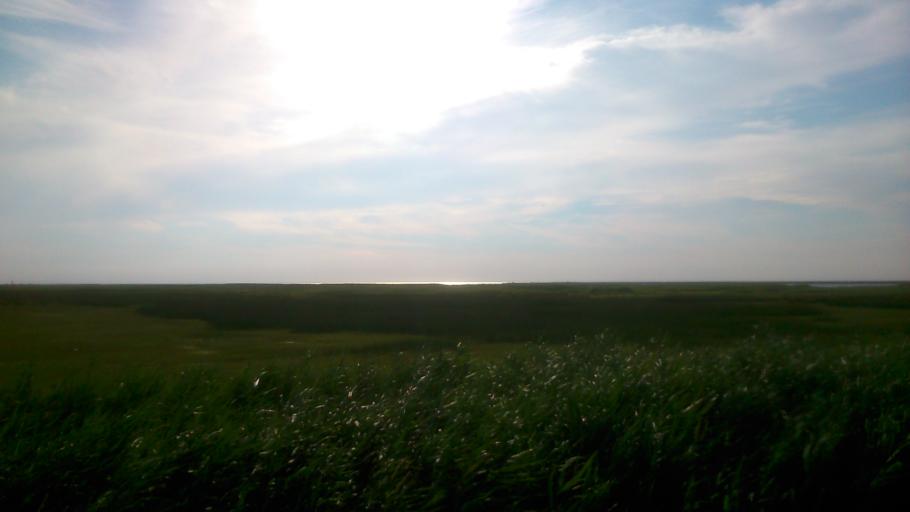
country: DK
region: Central Jutland
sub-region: Ringkobing-Skjern Kommune
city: Skjern
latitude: 55.9005
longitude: 8.3814
